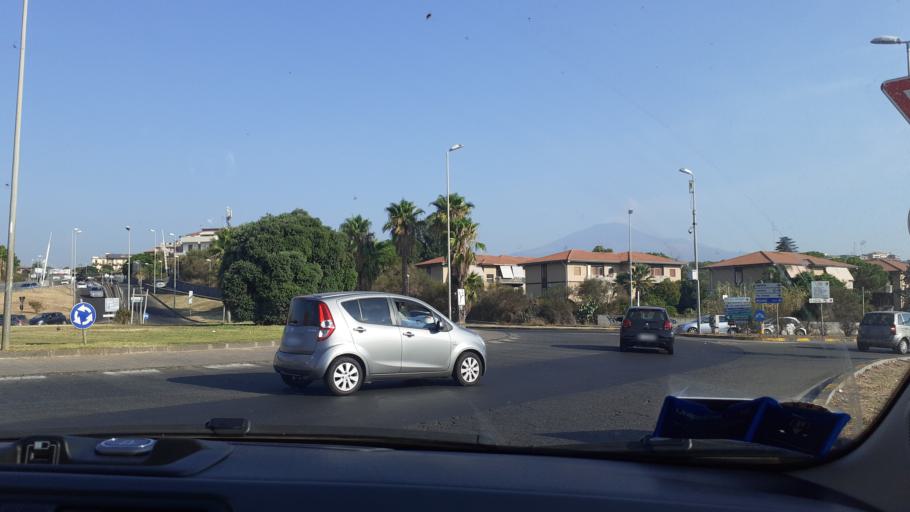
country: IT
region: Sicily
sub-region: Catania
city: Misterbianco
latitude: 37.5164
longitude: 15.0522
